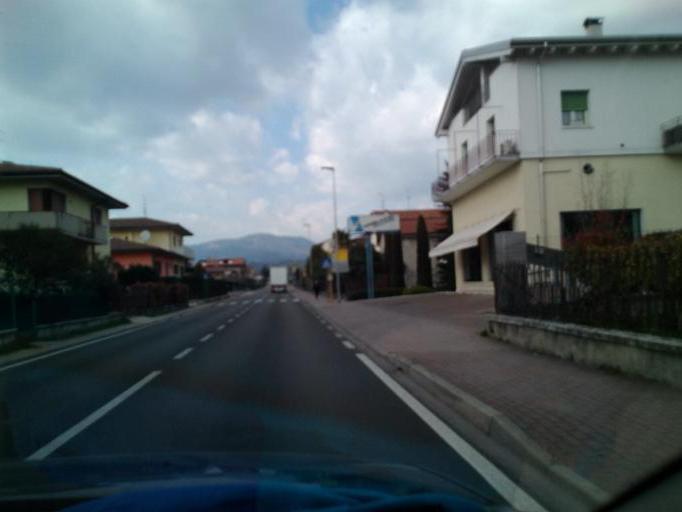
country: IT
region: Veneto
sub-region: Provincia di Verona
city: Pedemonte
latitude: 45.5048
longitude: 10.9163
